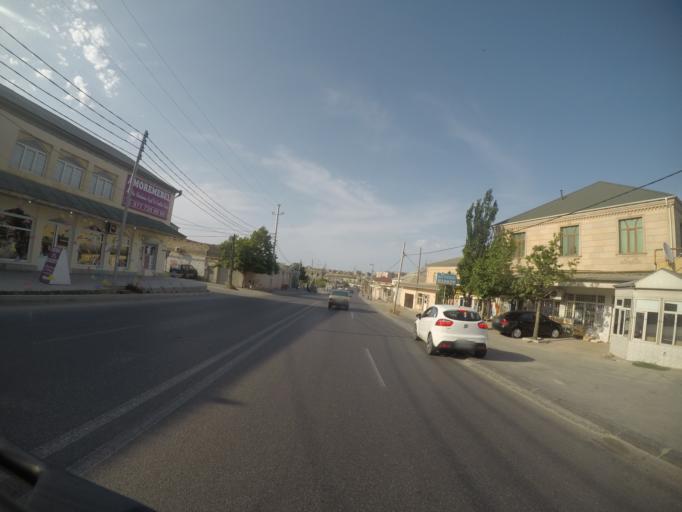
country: AZ
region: Baki
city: Binagadi
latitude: 40.4767
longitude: 49.8332
